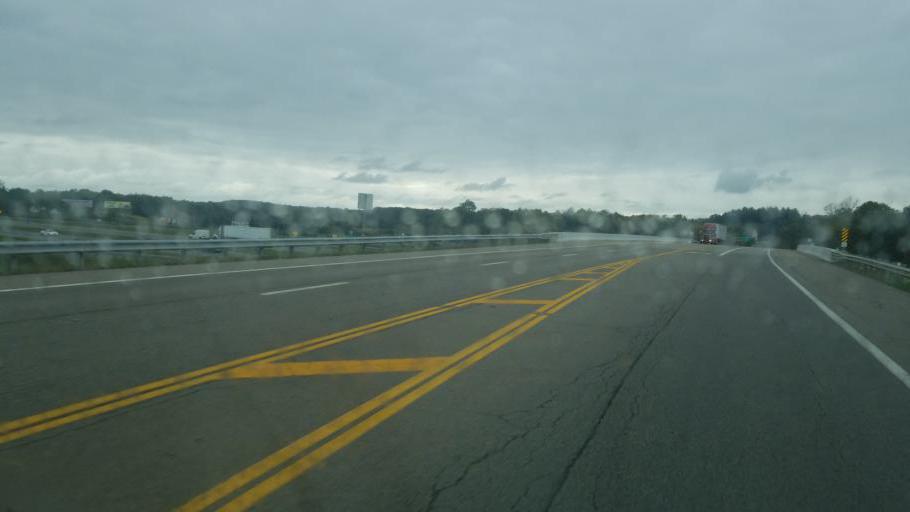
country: US
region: Ohio
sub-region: Richland County
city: Lincoln Heights
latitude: 40.7372
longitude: -82.4581
